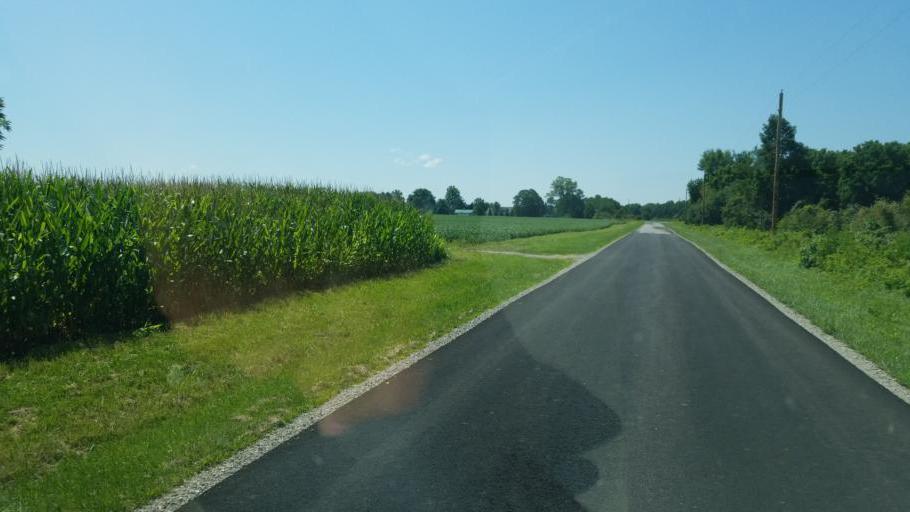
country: US
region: Ohio
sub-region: Delaware County
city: Ashley
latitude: 40.4311
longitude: -83.0398
